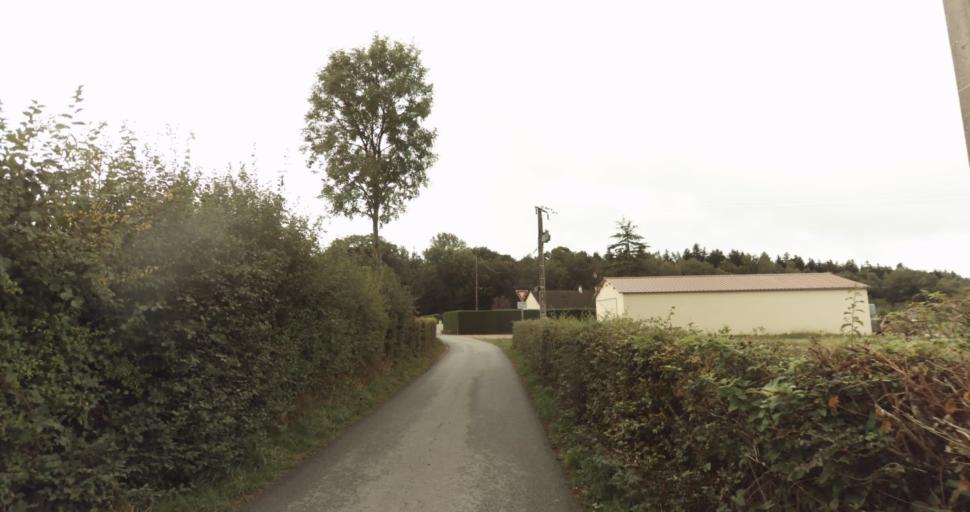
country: FR
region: Lower Normandy
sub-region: Departement de l'Orne
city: Gace
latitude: 48.8912
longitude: 0.3107
